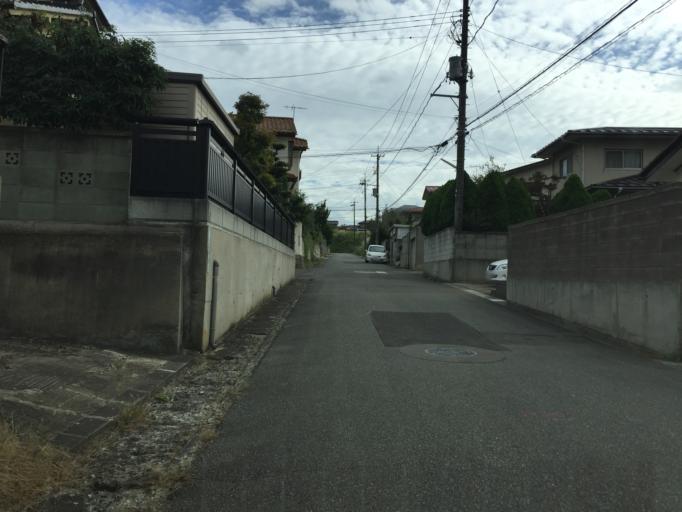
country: JP
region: Fukushima
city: Fukushima-shi
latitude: 37.6986
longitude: 140.4662
